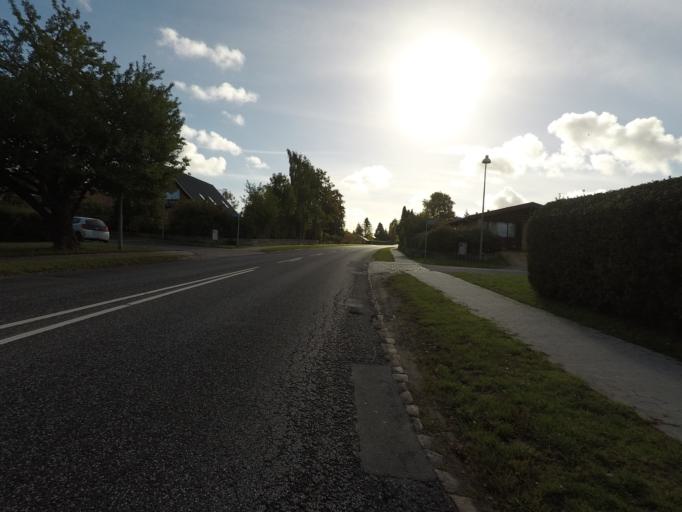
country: DK
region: Capital Region
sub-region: Egedal Kommune
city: Smorumnedre
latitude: 55.7380
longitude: 12.2937
